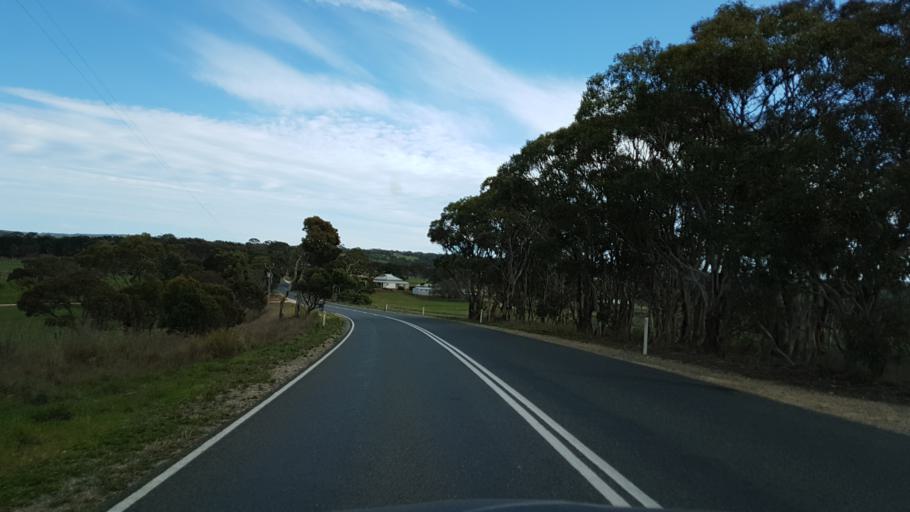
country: AU
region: South Australia
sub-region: Mount Barker
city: Macclesfield
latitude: -35.1498
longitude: 138.9361
